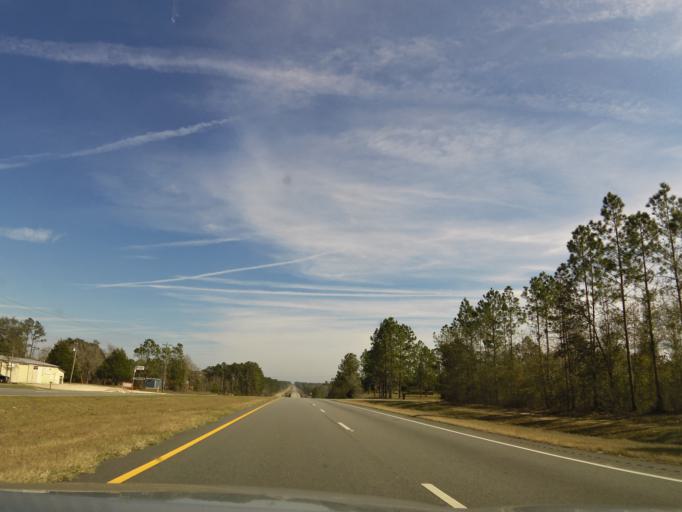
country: US
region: Georgia
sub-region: Brantley County
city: Nahunta
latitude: 31.2165
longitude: -81.8882
